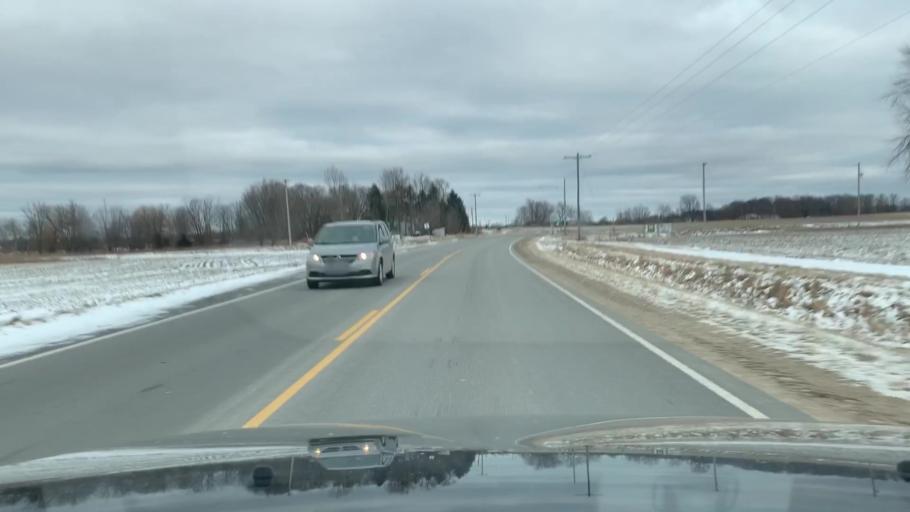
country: US
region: Michigan
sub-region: Ottawa County
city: Hudsonville
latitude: 42.8114
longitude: -85.9022
